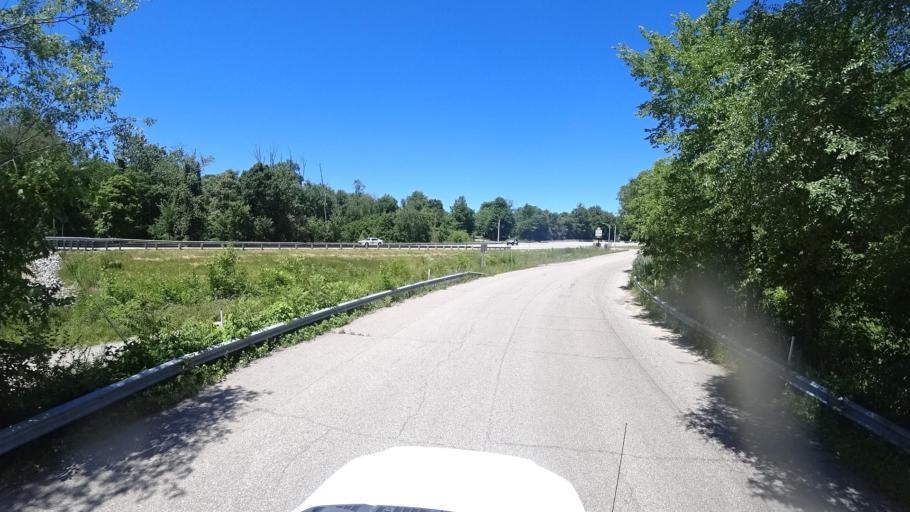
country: US
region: Indiana
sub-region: Porter County
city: Porter
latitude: 41.6221
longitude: -87.0868
